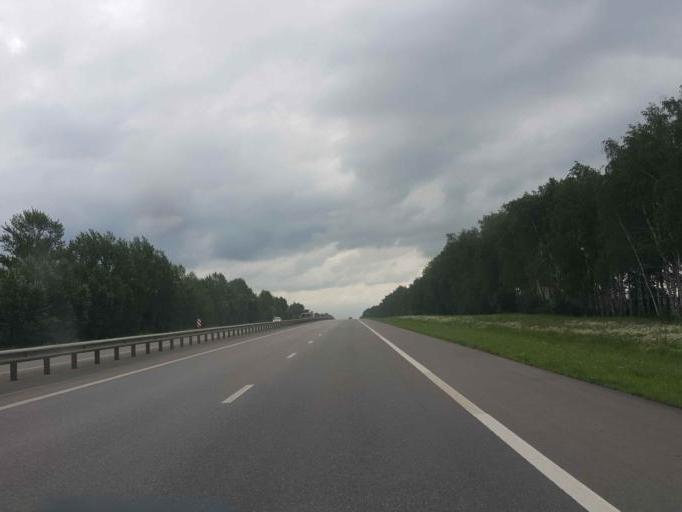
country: RU
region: Tambov
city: Selezni
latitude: 52.8129
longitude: 40.9484
